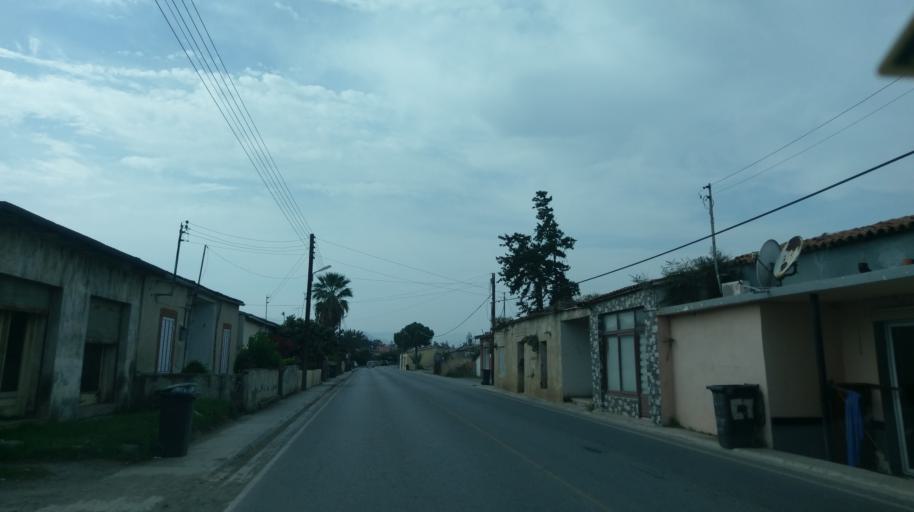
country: CY
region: Lefkosia
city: Lefka
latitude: 35.1544
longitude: 32.8825
